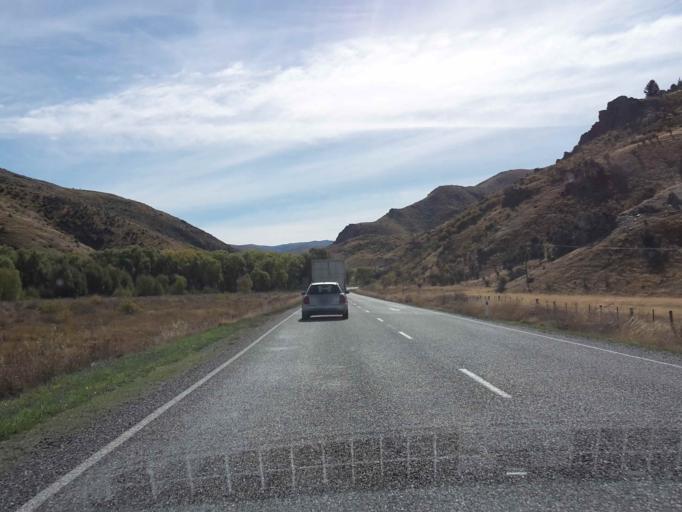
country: NZ
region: Otago
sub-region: Queenstown-Lakes District
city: Wanaka
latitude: -44.7470
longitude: 169.5096
